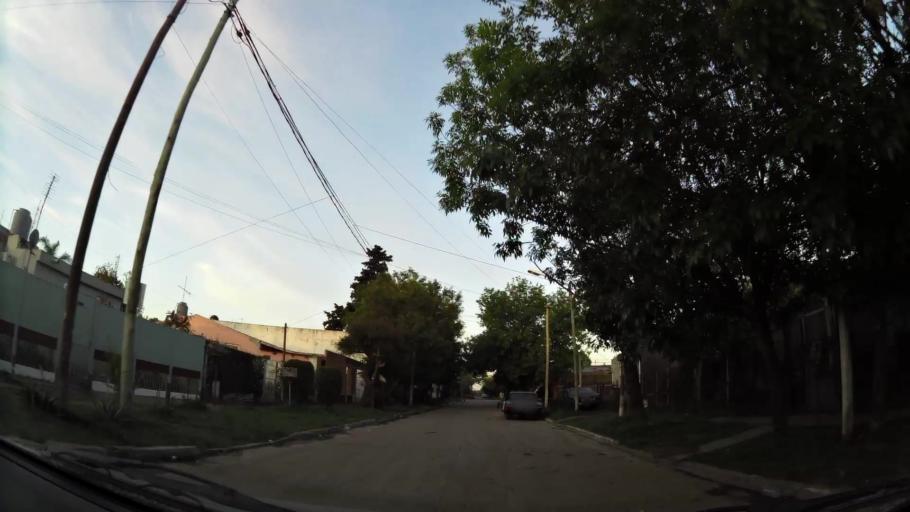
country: AR
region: Buenos Aires
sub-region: Partido de Quilmes
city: Quilmes
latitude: -34.7892
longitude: -58.2217
